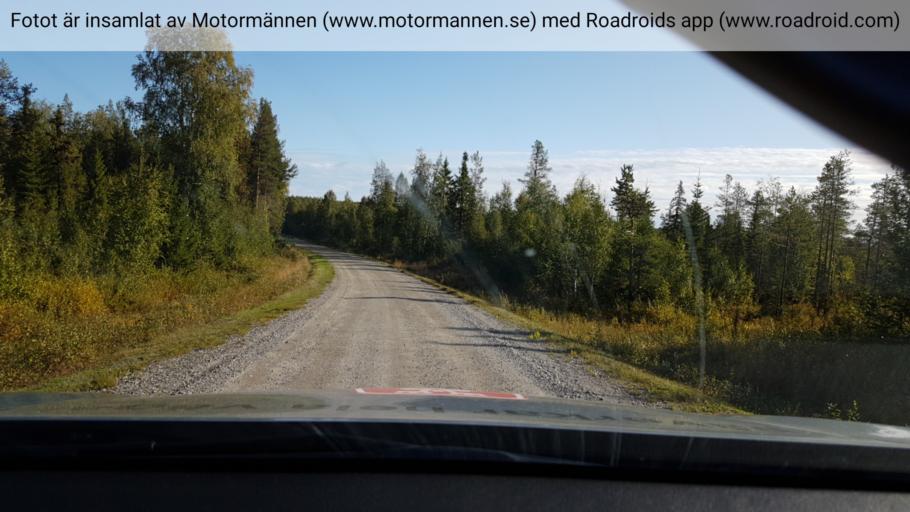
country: SE
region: Vaesterbotten
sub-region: Norsjo Kommun
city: Norsjoe
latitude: 64.6833
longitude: 19.4063
